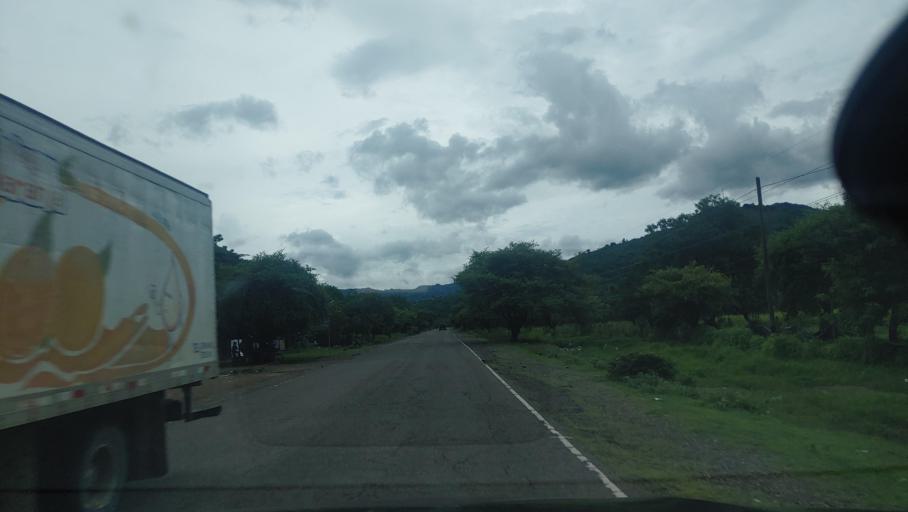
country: HN
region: Choluteca
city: Santa Ana de Yusguare
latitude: 13.3626
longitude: -87.0880
